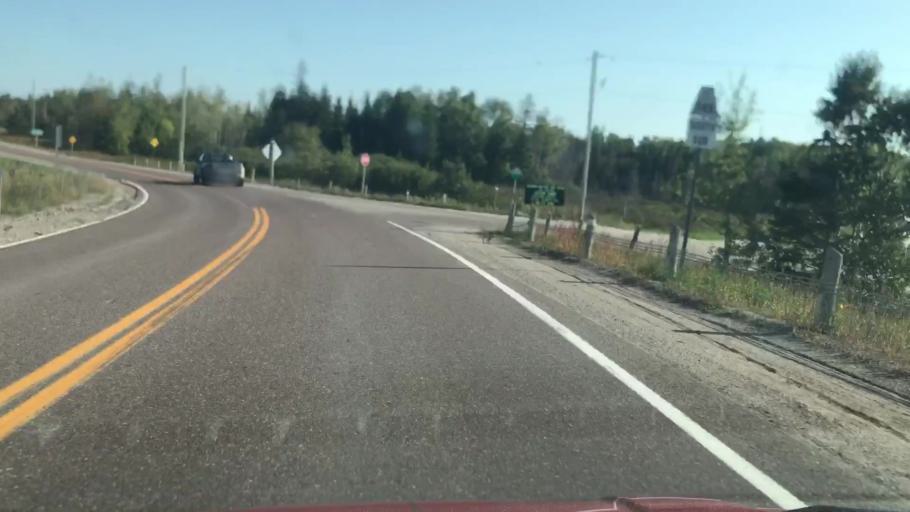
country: CA
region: Ontario
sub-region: Algoma
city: Sault Ste. Marie
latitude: 46.3371
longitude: -84.0095
